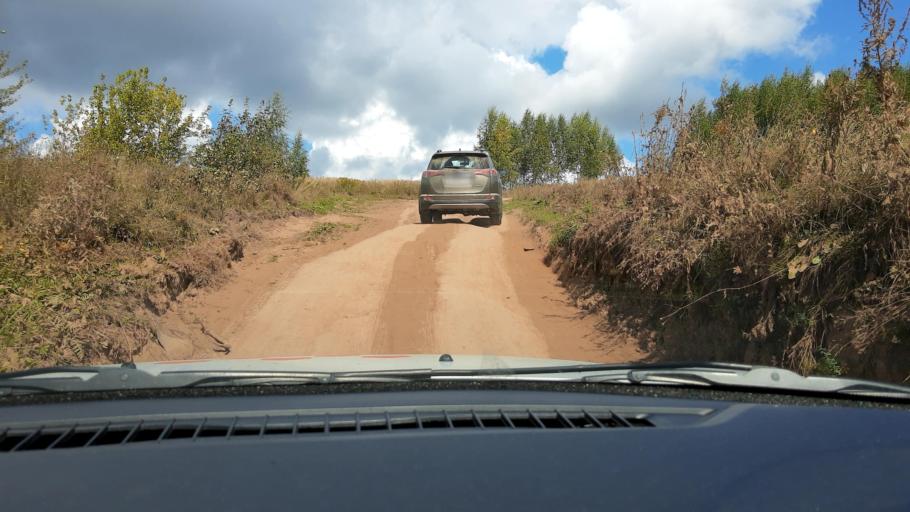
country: RU
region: Nizjnij Novgorod
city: Nizhniy Novgorod
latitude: 56.1993
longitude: 43.9633
